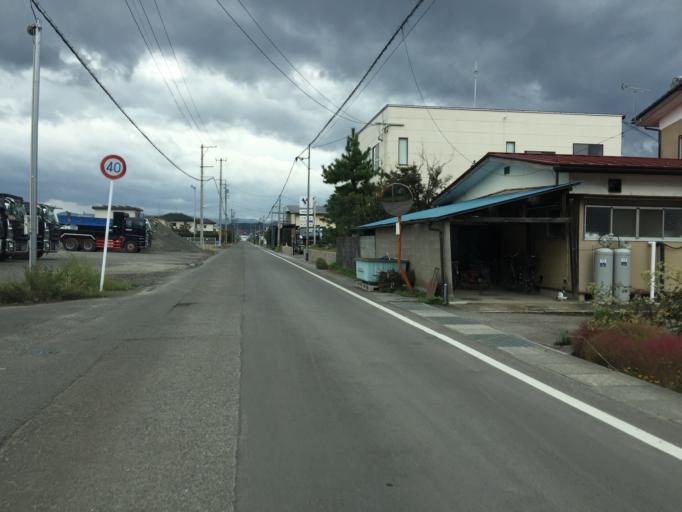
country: JP
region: Fukushima
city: Hobaramachi
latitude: 37.8271
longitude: 140.5456
